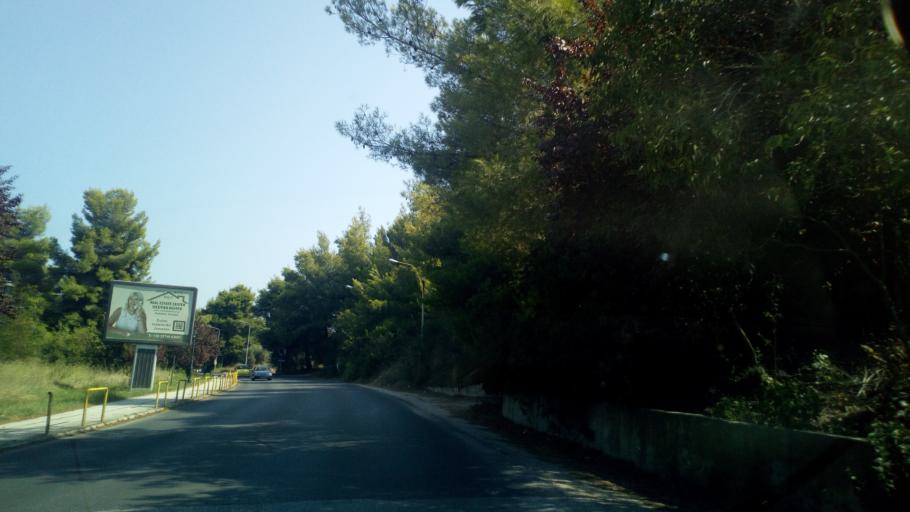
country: GR
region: Central Macedonia
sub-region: Nomos Chalkidikis
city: Kallithea
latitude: 40.0719
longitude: 23.4501
